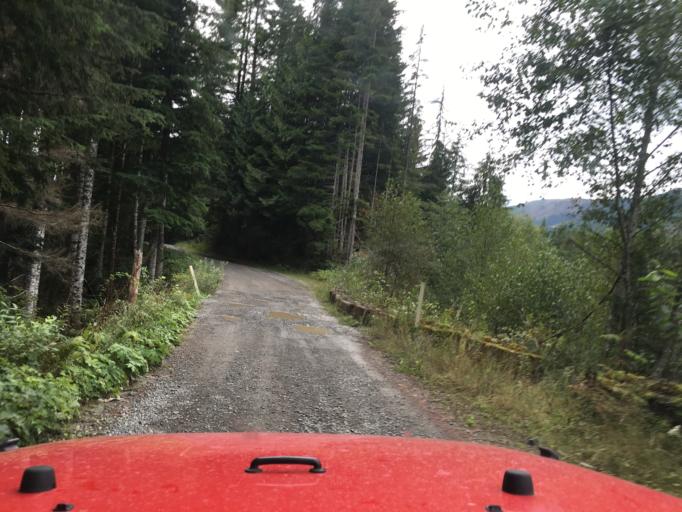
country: US
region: Washington
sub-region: Snohomish County
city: Gold Bar
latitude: 47.6573
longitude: -121.6326
